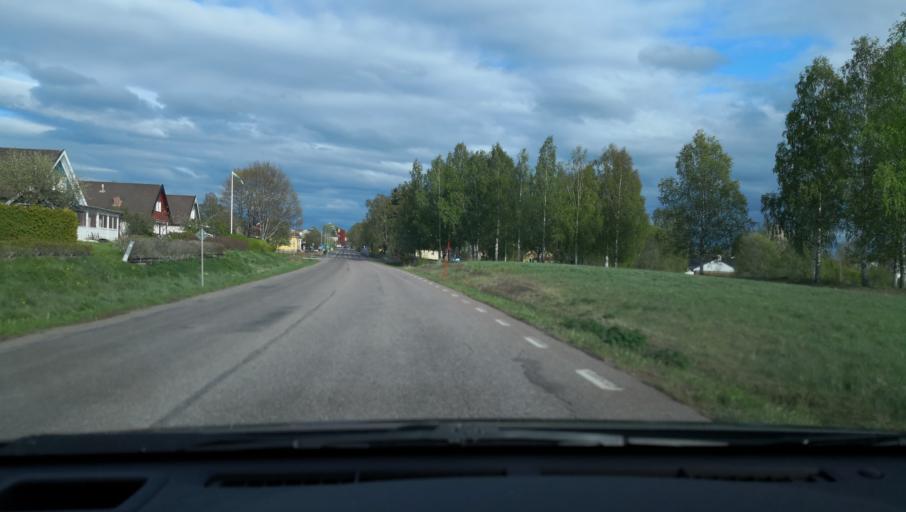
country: SE
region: Dalarna
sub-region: Hedemora Kommun
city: Hedemora
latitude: 60.2796
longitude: 15.9700
